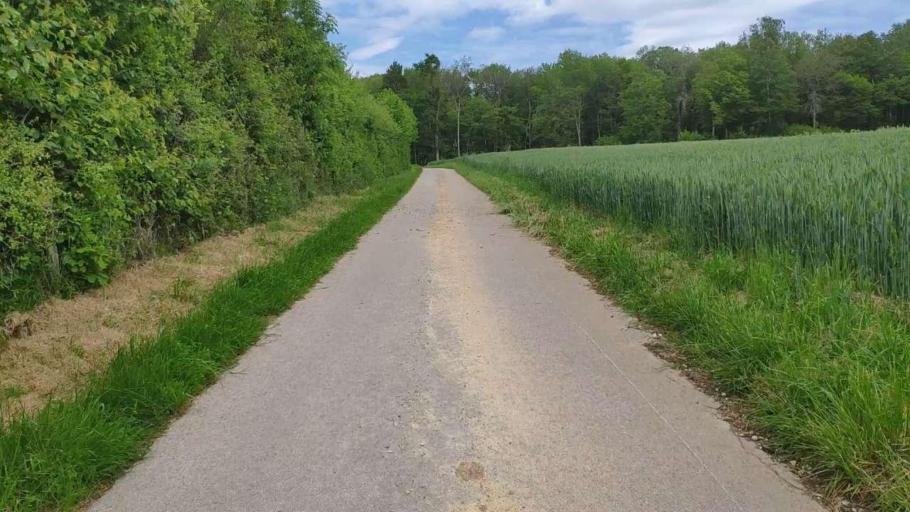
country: FR
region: Franche-Comte
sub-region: Departement du Jura
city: Poligny
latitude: 46.7697
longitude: 5.6558
